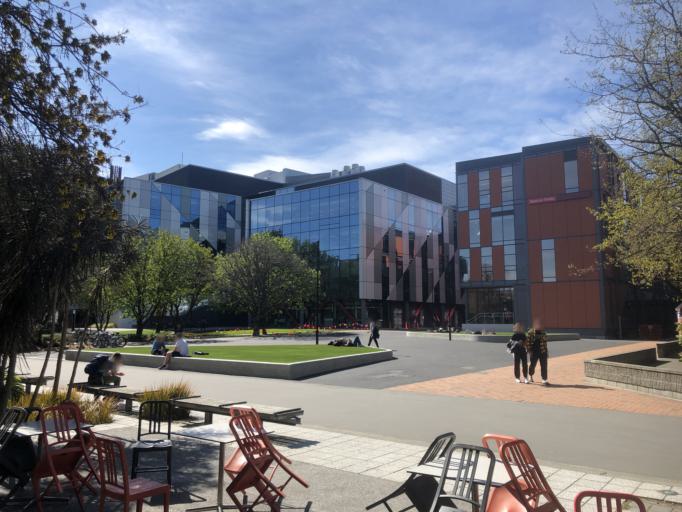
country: NZ
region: Canterbury
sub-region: Christchurch City
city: Christchurch
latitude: -43.5234
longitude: 172.5830
